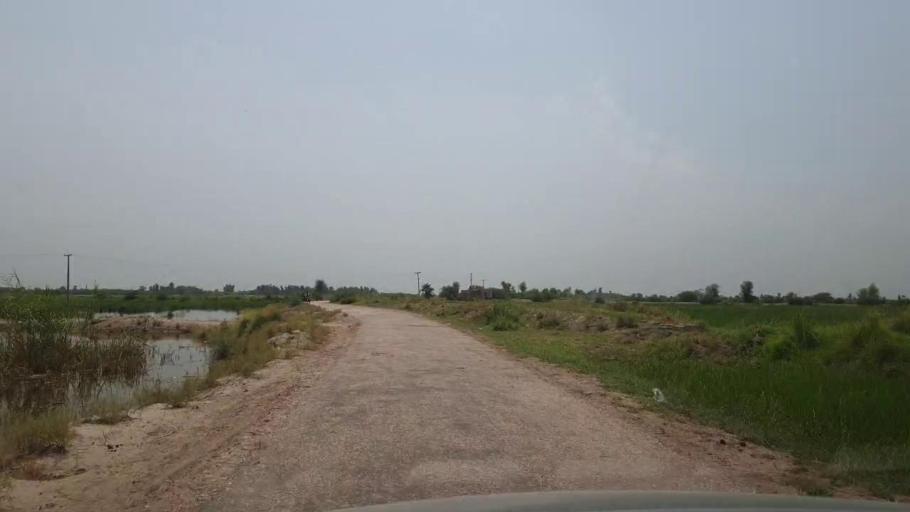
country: PK
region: Sindh
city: Garhi Yasin
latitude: 27.8858
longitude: 68.4950
